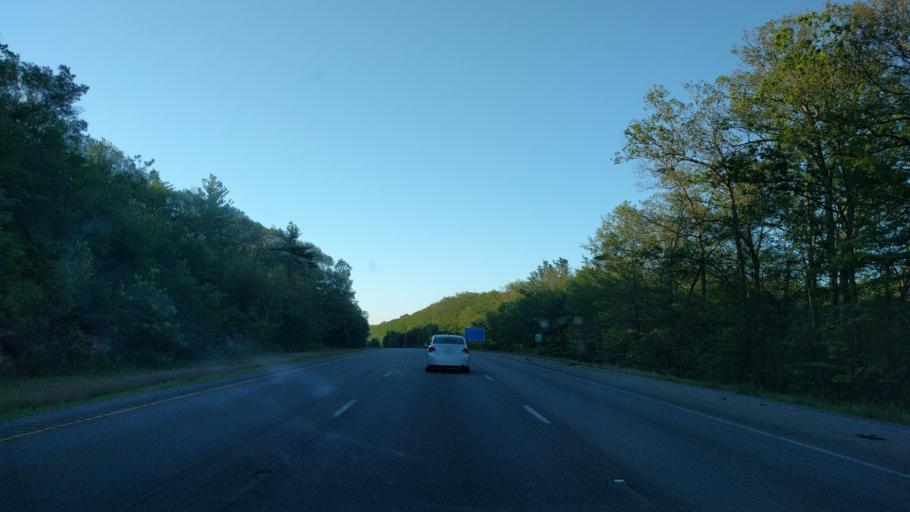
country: US
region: Massachusetts
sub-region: Middlesex County
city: Hopkinton
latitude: 42.1881
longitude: -71.5351
